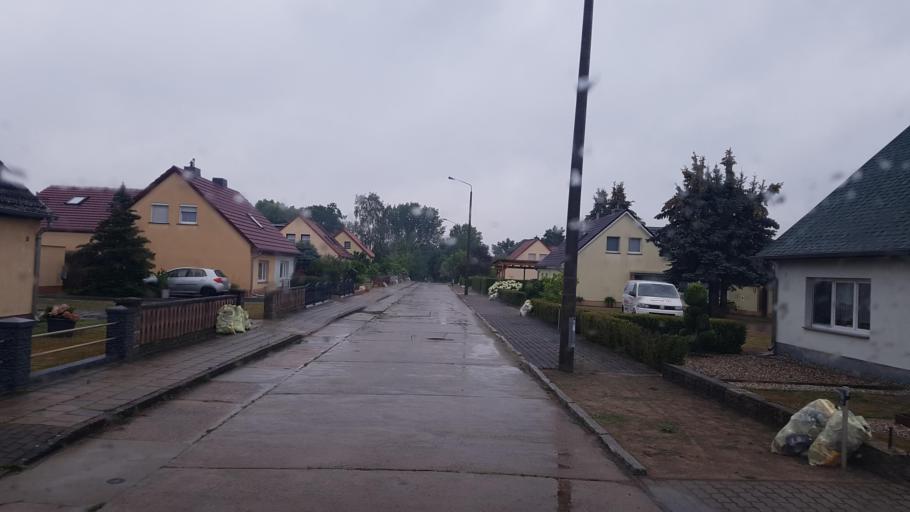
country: DE
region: Brandenburg
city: Juterbog
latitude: 52.0064
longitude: 13.0833
